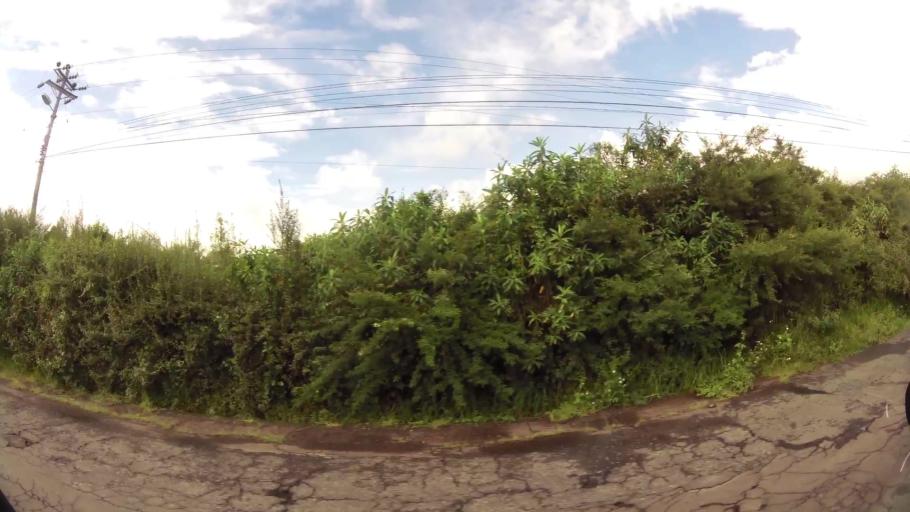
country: EC
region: Pichincha
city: Sangolqui
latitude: -0.3134
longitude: -78.4079
